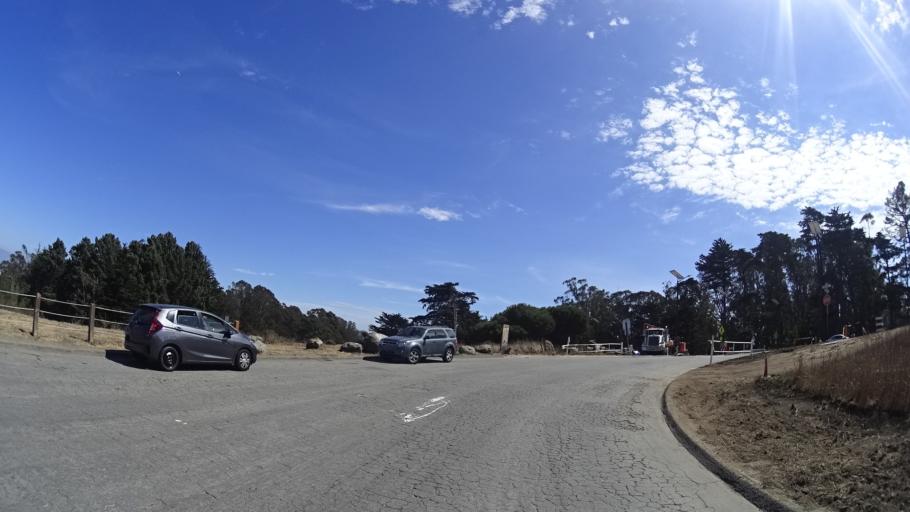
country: US
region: California
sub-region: San Mateo County
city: Brisbane
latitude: 37.7192
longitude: -122.4187
